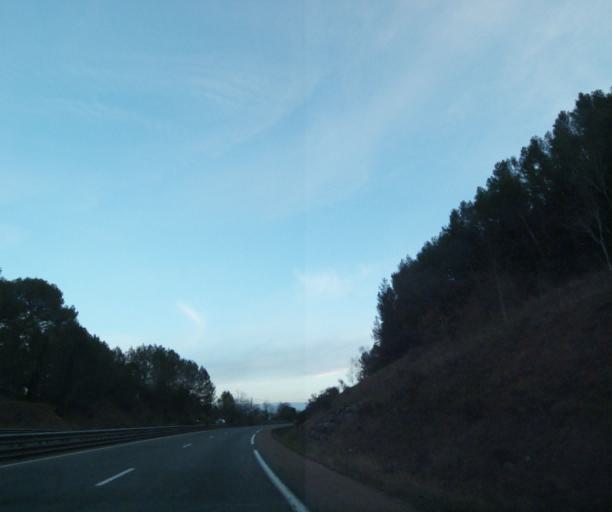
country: FR
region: Provence-Alpes-Cote d'Azur
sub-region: Departement du Var
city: Trans-en-Provence
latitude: 43.4931
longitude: 6.5040
